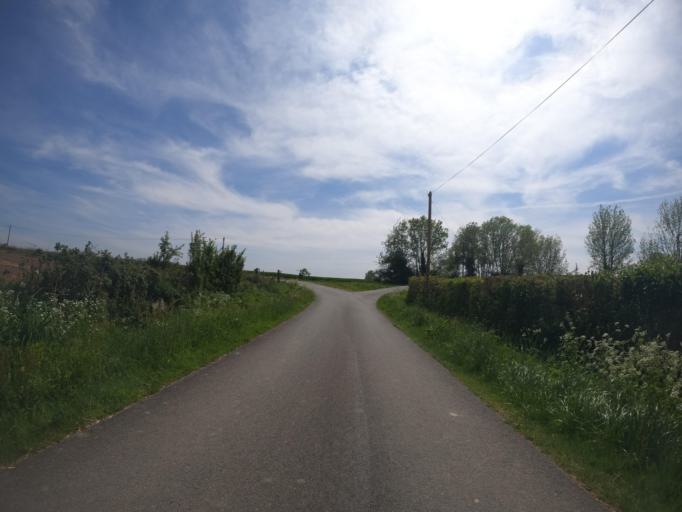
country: FR
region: Poitou-Charentes
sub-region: Departement des Deux-Sevres
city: Secondigny
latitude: 46.6485
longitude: -0.4981
